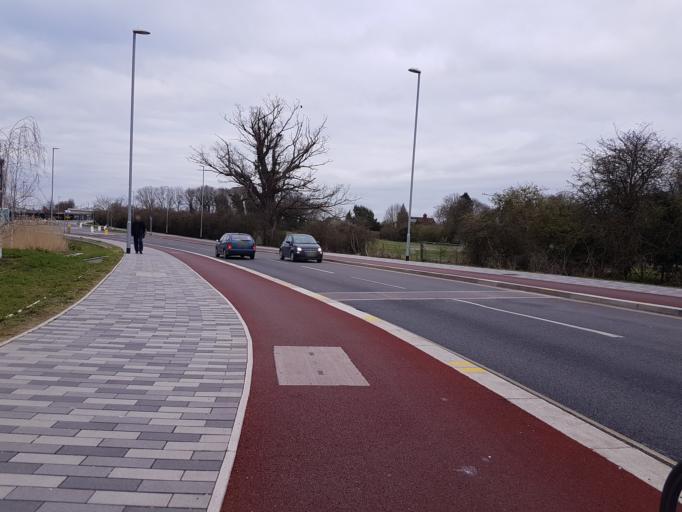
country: GB
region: England
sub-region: Cambridgeshire
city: Girton
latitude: 52.2155
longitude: 0.0865
